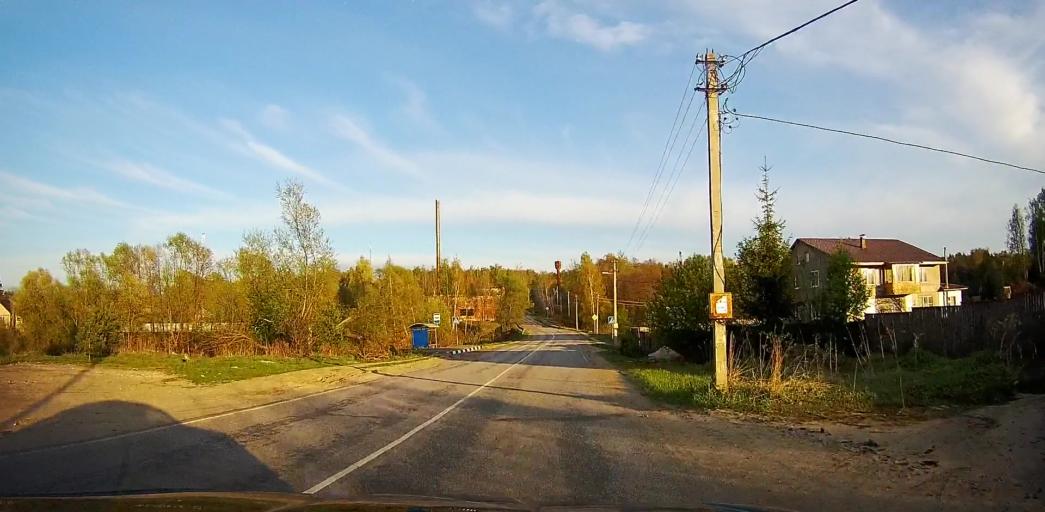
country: RU
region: Moskovskaya
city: Meshcherino
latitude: 55.2308
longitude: 38.3680
